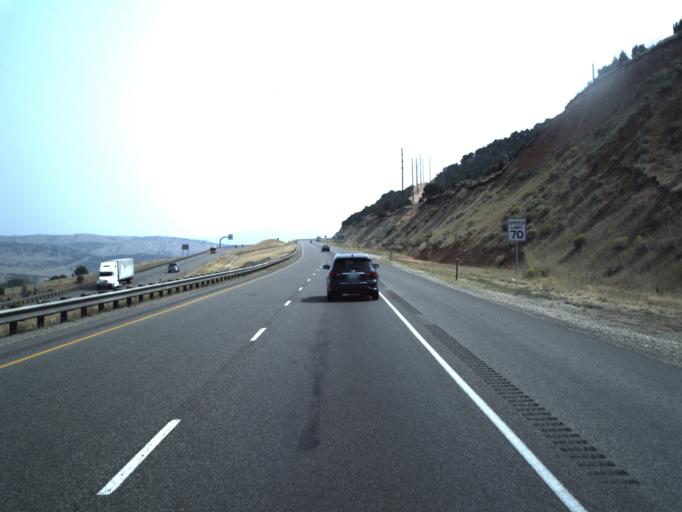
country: US
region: Utah
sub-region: Summit County
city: Coalville
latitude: 40.9625
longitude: -111.4326
